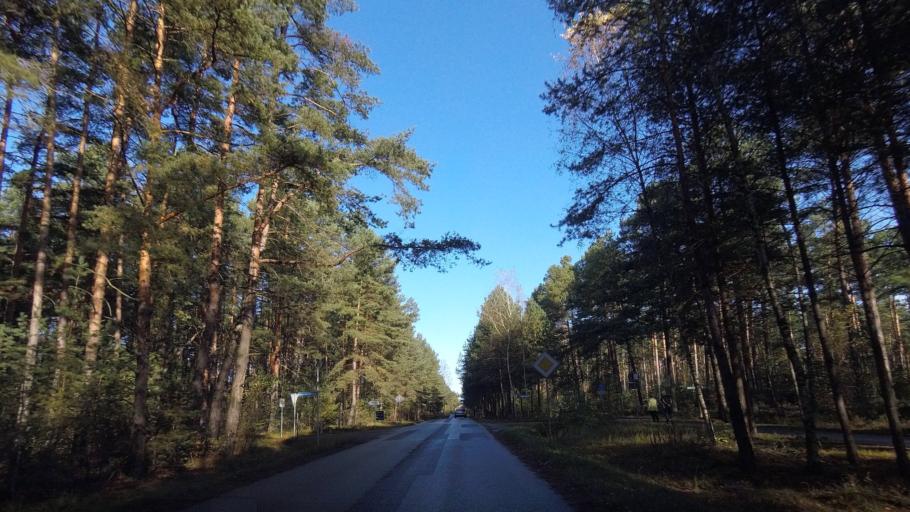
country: DE
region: Brandenburg
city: Borkwalde
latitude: 52.2608
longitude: 12.8348
